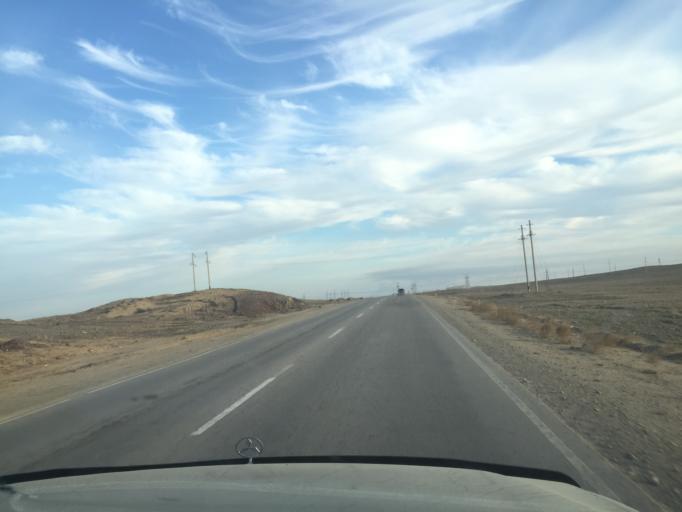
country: KZ
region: Almaty Oblysy
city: Ulken
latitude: 45.1978
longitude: 73.9004
